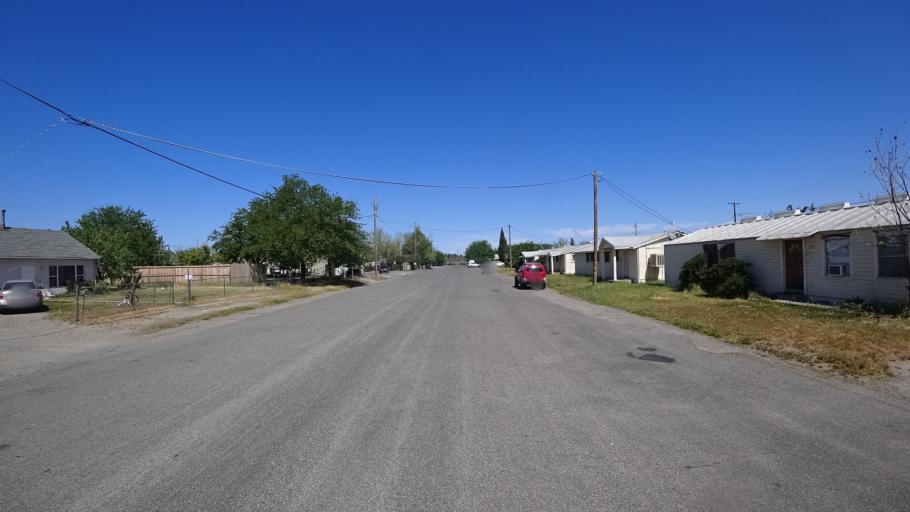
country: US
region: California
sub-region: Glenn County
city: Orland
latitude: 39.7524
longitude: -122.1954
